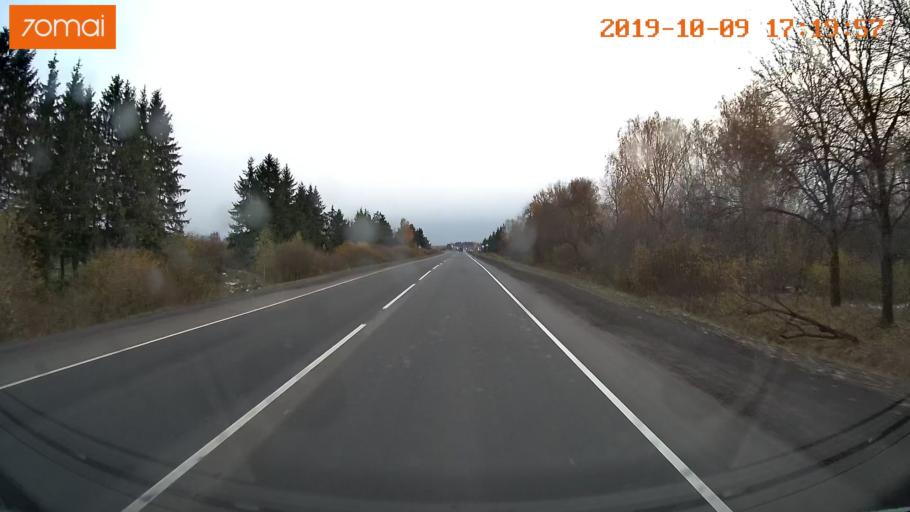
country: RU
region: Ivanovo
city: Furmanov
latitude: 57.2400
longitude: 41.1468
